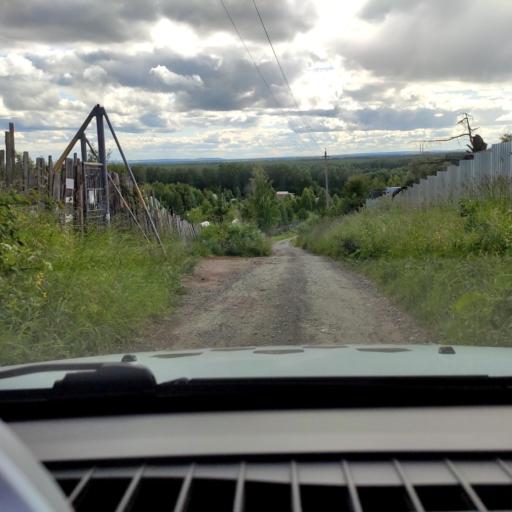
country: RU
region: Perm
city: Overyata
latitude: 58.1007
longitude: 55.8610
